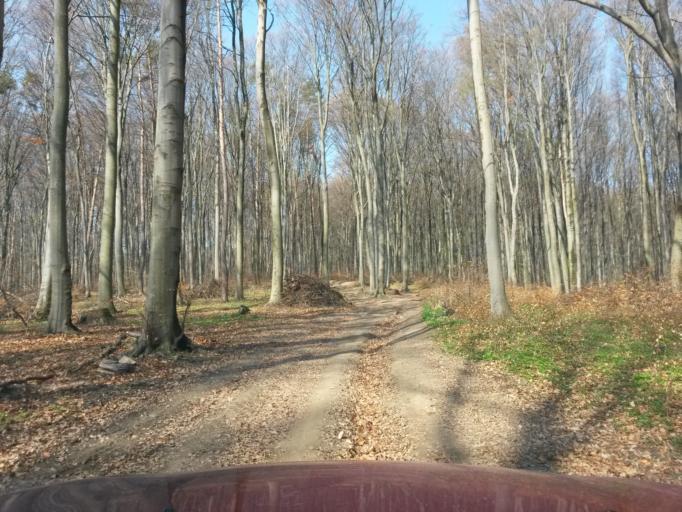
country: SK
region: Presovsky
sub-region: Okres Presov
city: Presov
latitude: 48.9271
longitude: 21.1596
